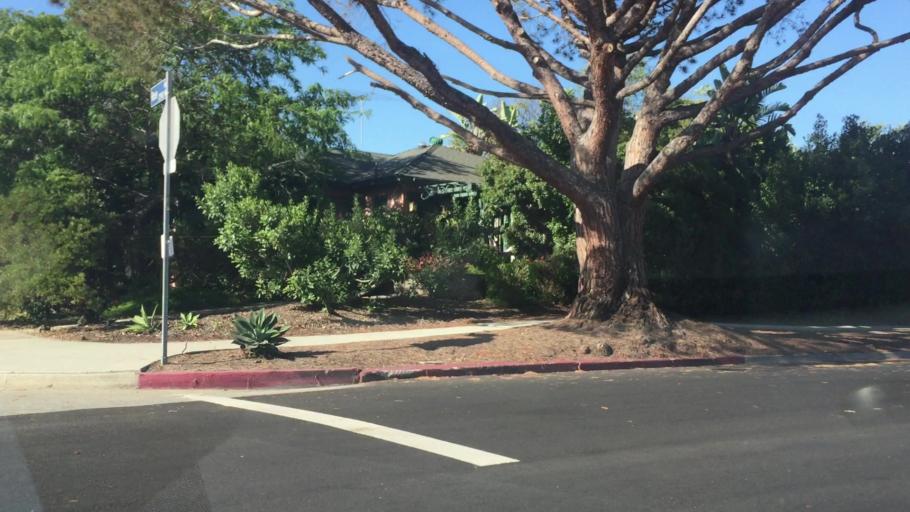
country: US
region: California
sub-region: Los Angeles County
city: Marina del Rey
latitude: 34.0100
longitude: -118.4496
